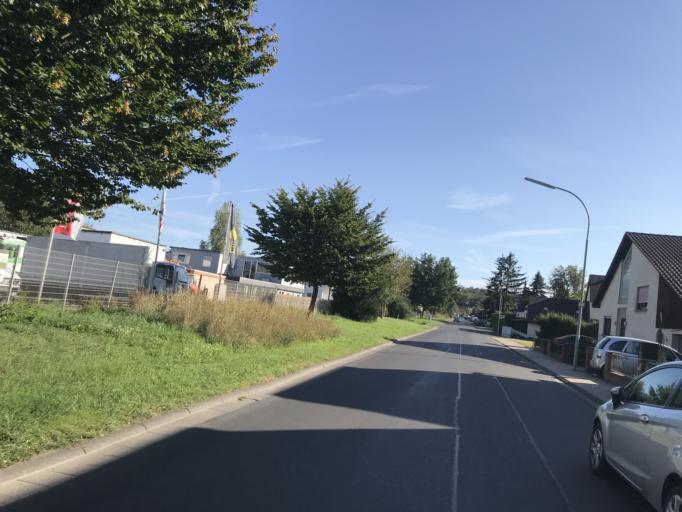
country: DE
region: Hesse
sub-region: Regierungsbezirk Darmstadt
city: Altenstadt
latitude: 50.2735
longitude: 8.9629
